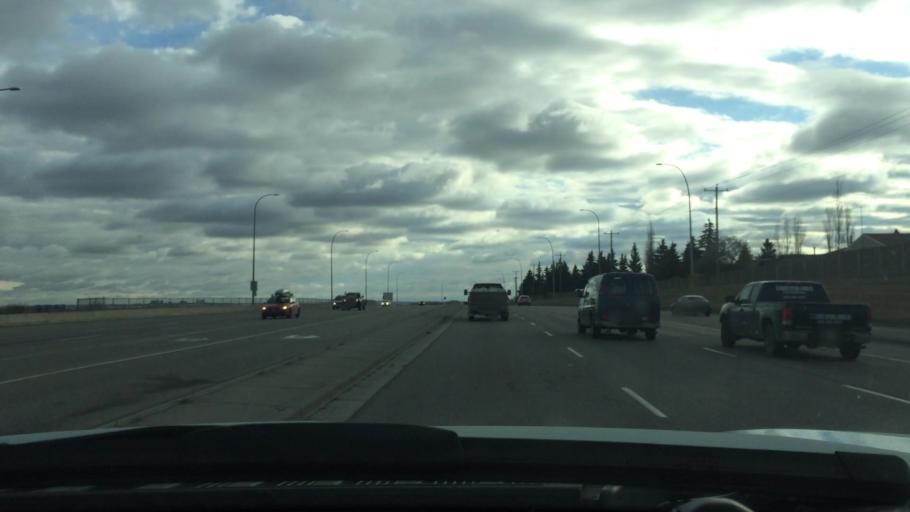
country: CA
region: Alberta
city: Calgary
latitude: 51.1380
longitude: -114.0810
